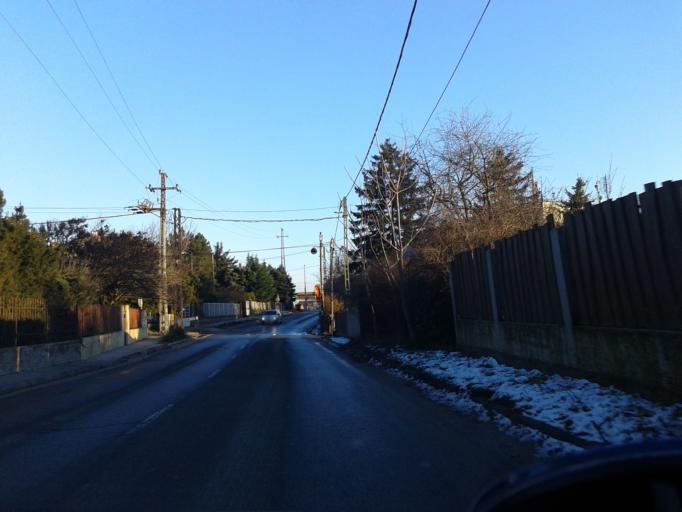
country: HU
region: Pest
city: Diosd
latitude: 47.4119
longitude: 18.9555
